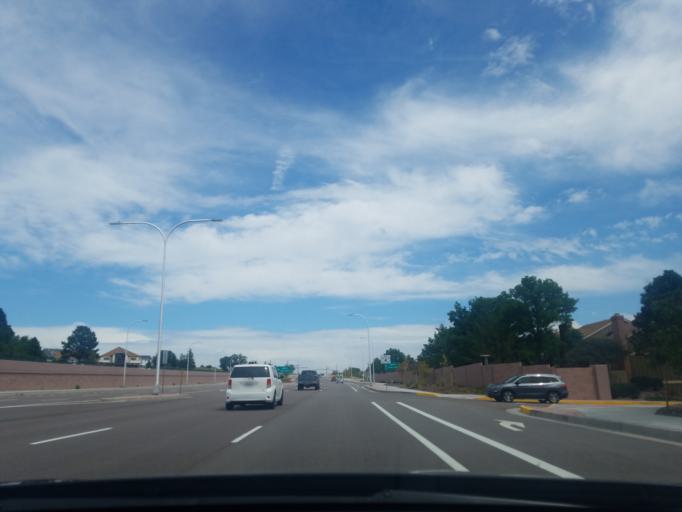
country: US
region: Colorado
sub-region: El Paso County
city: Air Force Academy
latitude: 38.9330
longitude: -104.7811
